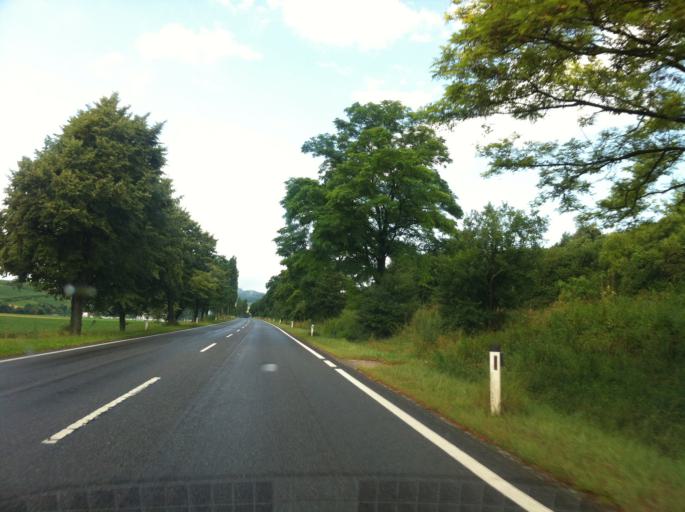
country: AT
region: Lower Austria
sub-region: Politischer Bezirk Tulln
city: Sieghartskirchen
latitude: 48.2527
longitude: 16.0356
